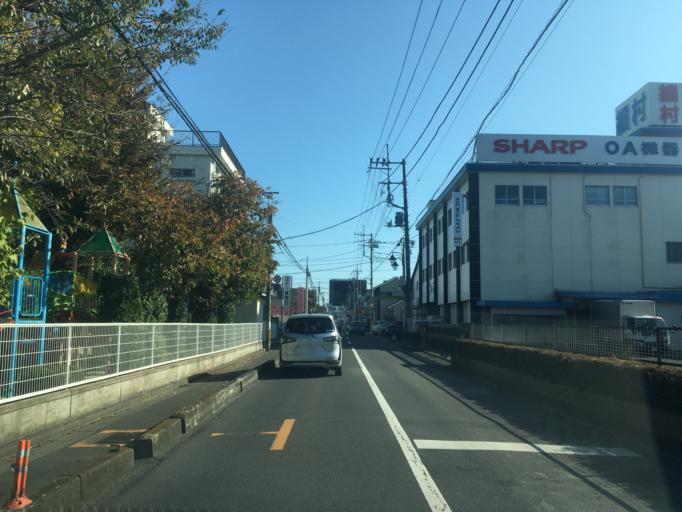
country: JP
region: Saitama
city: Kawagoe
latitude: 35.8997
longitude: 139.4702
